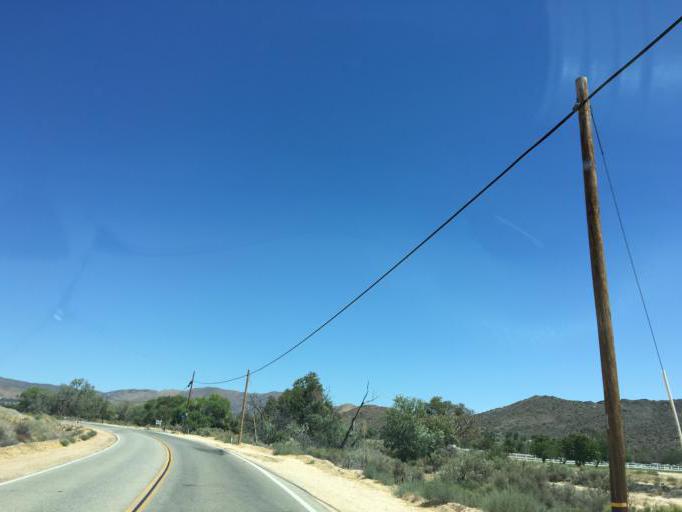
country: US
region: California
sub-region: Los Angeles County
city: Acton
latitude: 34.4566
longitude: -118.1968
